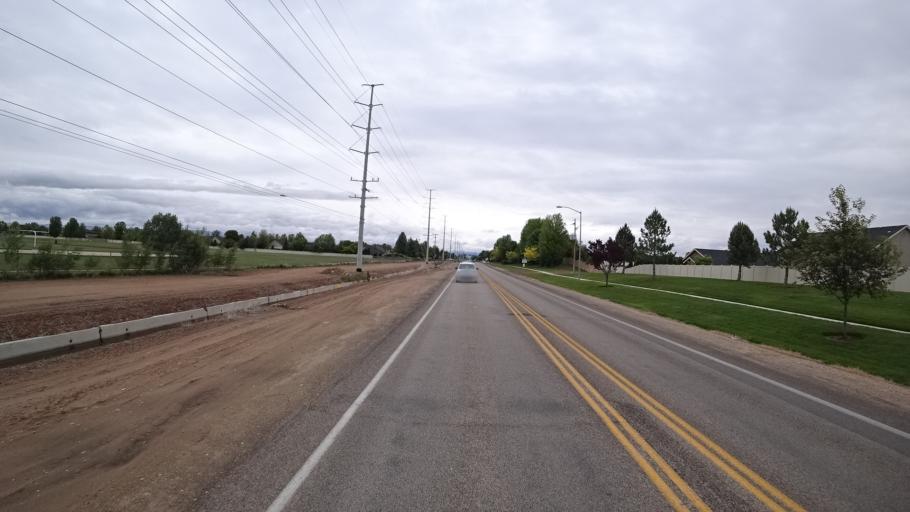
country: US
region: Idaho
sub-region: Ada County
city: Meridian
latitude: 43.6484
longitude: -116.3889
